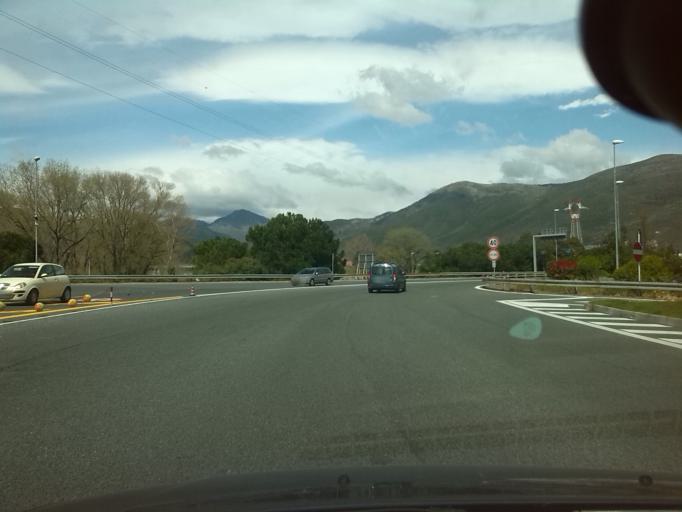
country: IT
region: Liguria
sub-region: Provincia di Savona
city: San Fedele-Lusignano
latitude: 44.0625
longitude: 8.1779
